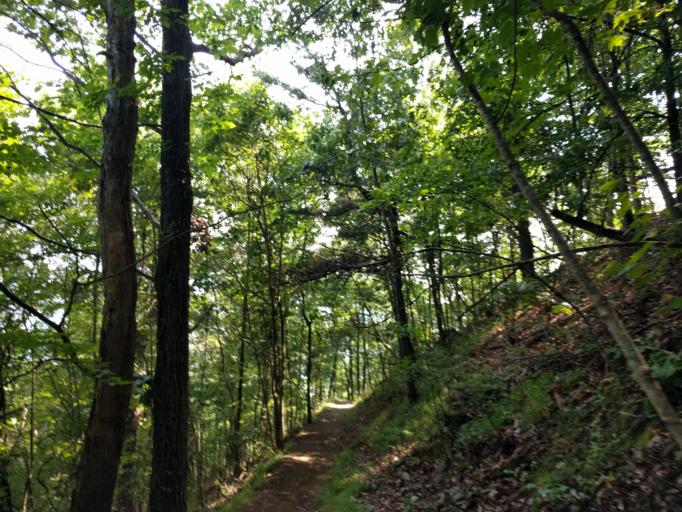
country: US
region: Virginia
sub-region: Smyth County
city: Marion
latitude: 36.8826
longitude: -81.5082
